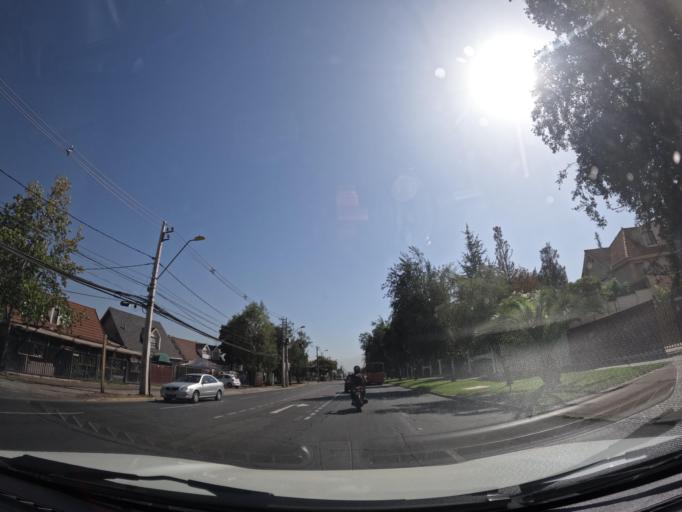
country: CL
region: Santiago Metropolitan
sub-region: Provincia de Santiago
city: Villa Presidente Frei, Nunoa, Santiago, Chile
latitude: -33.4821
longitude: -70.5458
